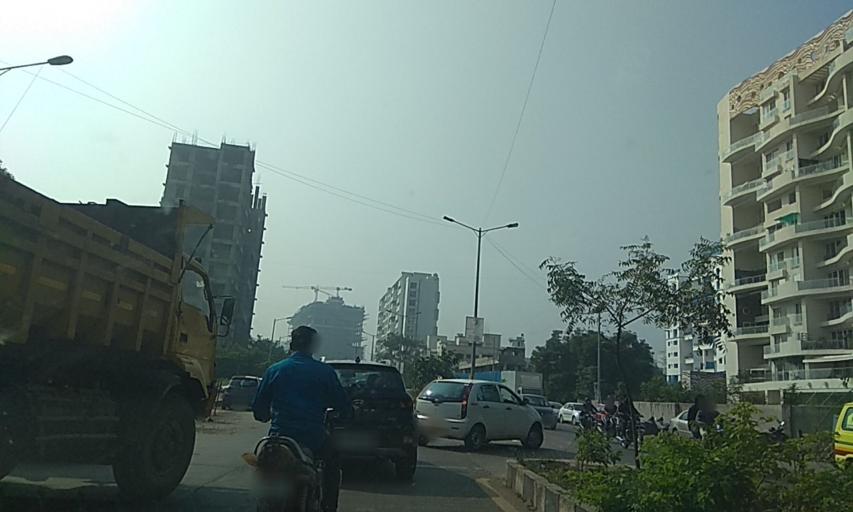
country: IN
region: Maharashtra
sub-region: Pune Division
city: Pimpri
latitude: 18.5619
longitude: 73.7767
